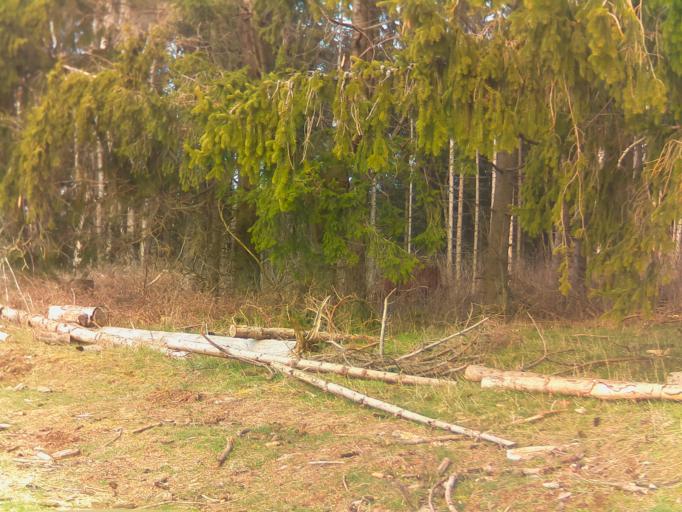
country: DE
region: Saarland
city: Nonnweiler
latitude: 49.5567
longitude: 6.9862
